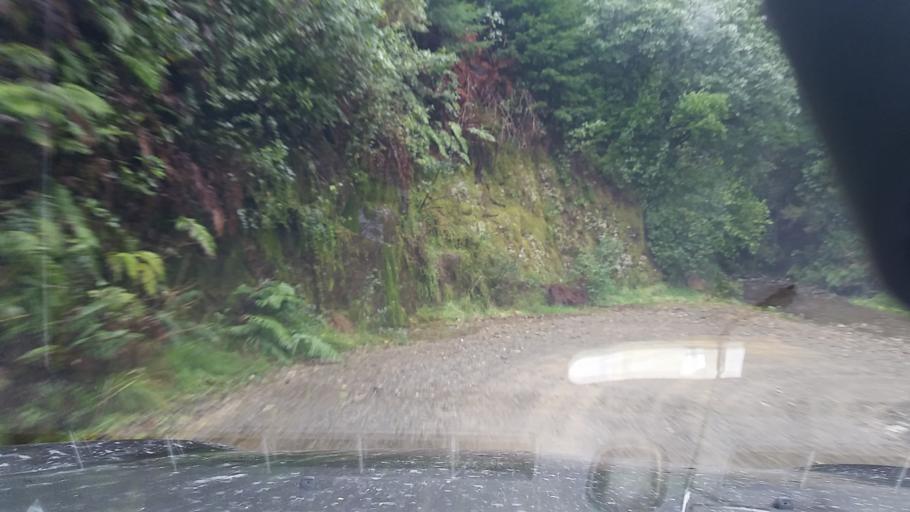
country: NZ
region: Nelson
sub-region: Nelson City
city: Nelson
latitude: -41.3709
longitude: 173.6097
